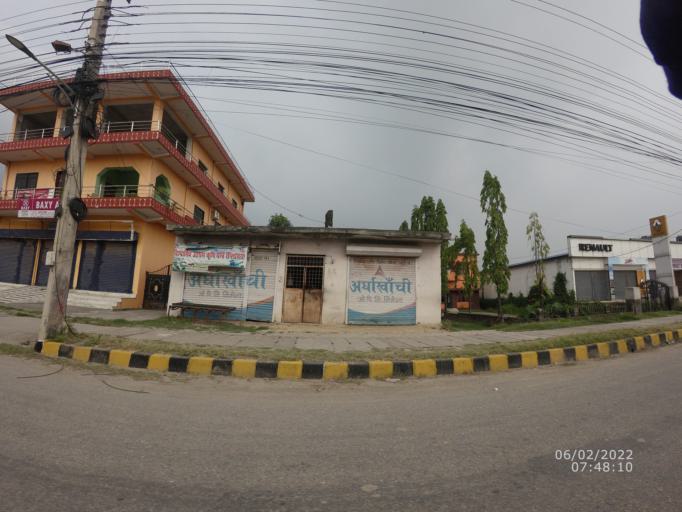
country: NP
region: Western Region
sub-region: Lumbini Zone
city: Bhairahawa
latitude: 27.5249
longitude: 83.4554
